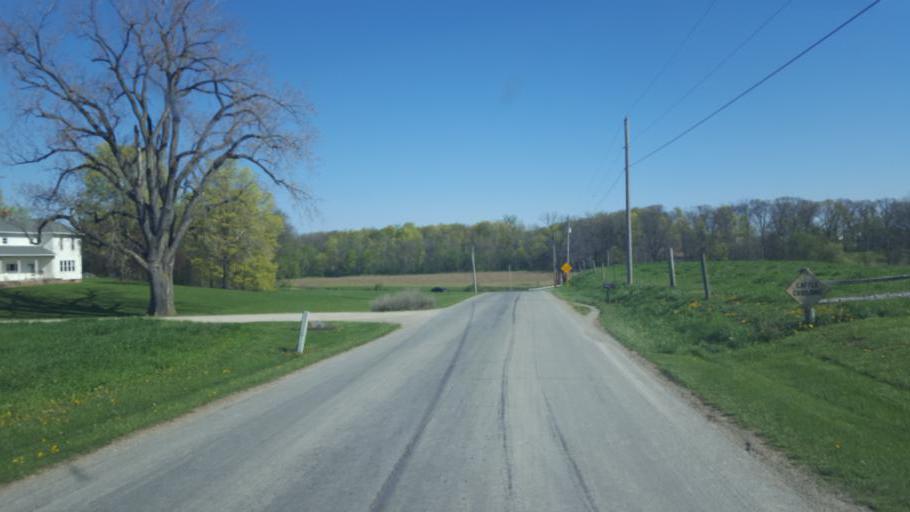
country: US
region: Ohio
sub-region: Wyandot County
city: Upper Sandusky
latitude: 40.8871
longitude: -83.2228
